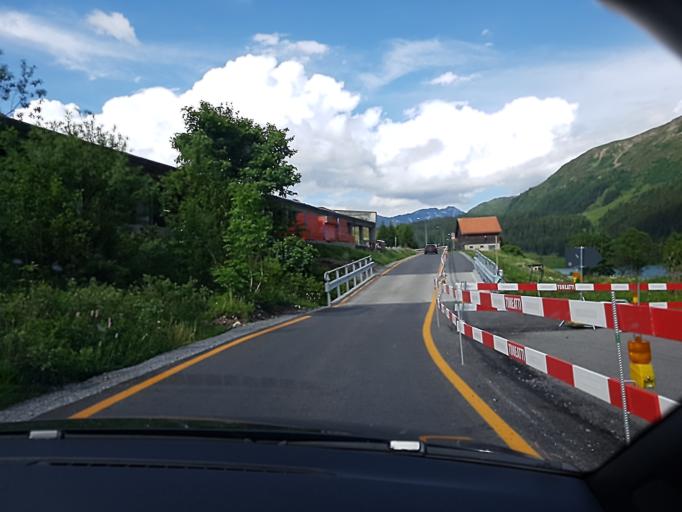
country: CH
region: Grisons
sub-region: Praettigau/Davos District
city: Davos
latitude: 46.8172
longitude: 9.8460
